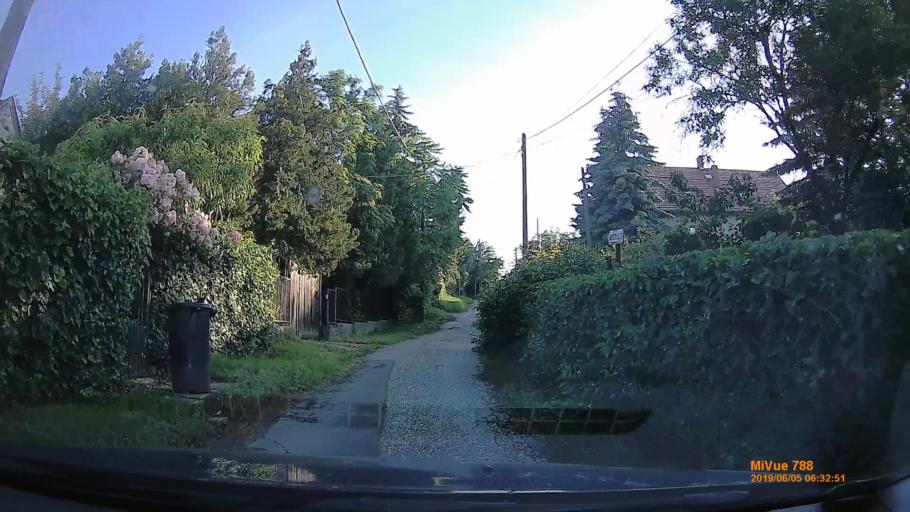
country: HU
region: Pest
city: Urom
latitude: 47.5727
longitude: 19.0249
